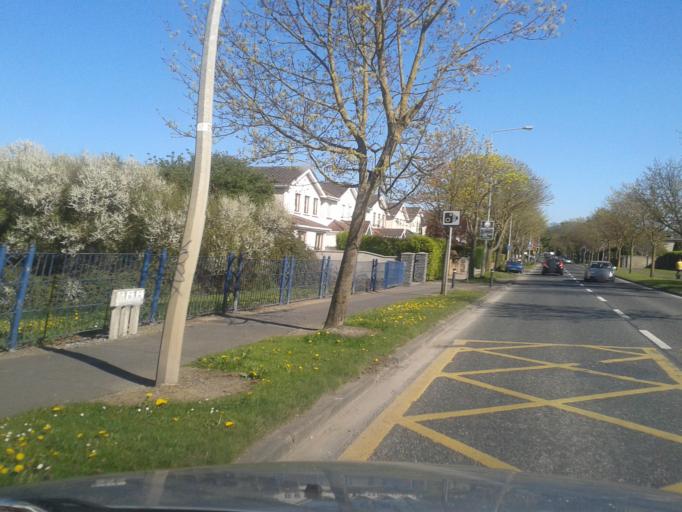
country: IE
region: Leinster
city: Kinsealy-Drinan
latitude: 53.4482
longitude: -6.1798
